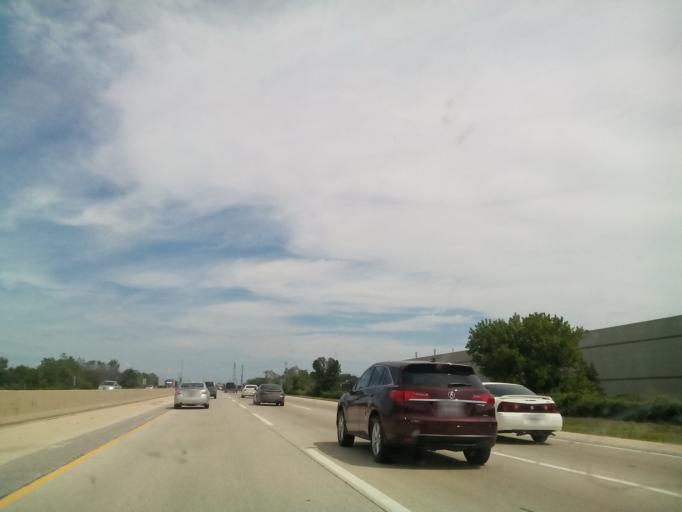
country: US
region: Illinois
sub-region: Kane County
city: North Aurora
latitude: 41.7997
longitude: -88.2598
